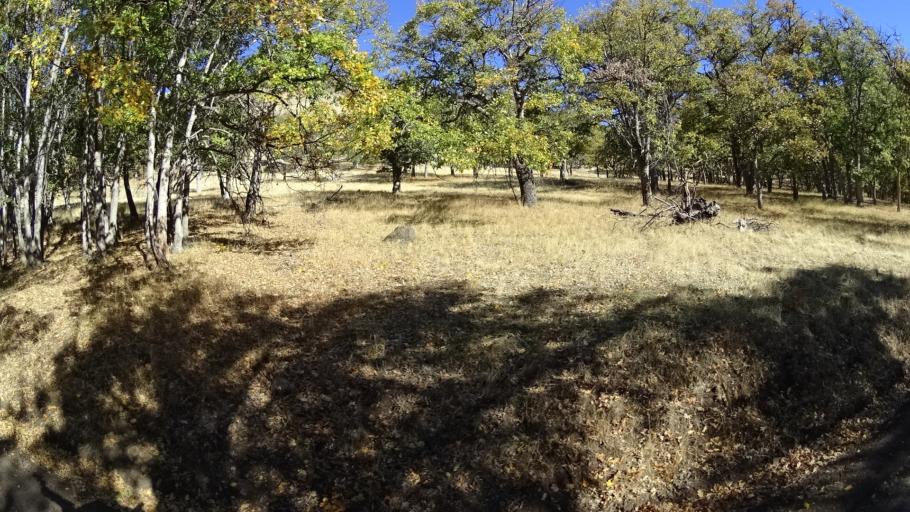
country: US
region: California
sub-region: Siskiyou County
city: Montague
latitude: 41.9842
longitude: -122.2987
